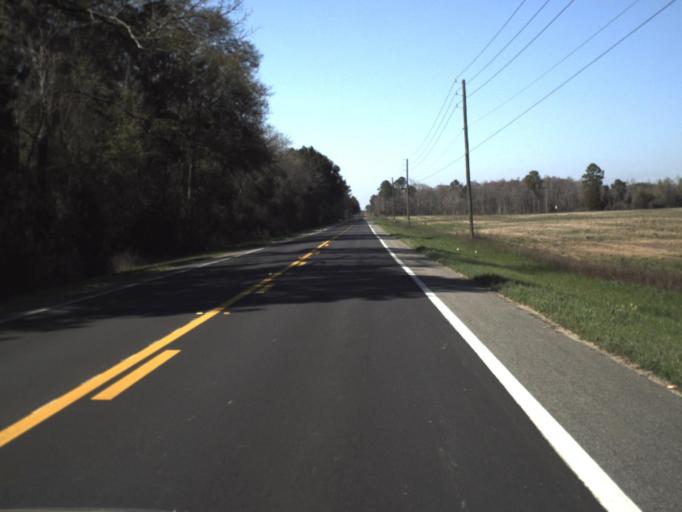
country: US
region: Florida
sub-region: Jackson County
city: Marianna
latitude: 30.6686
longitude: -85.1680
